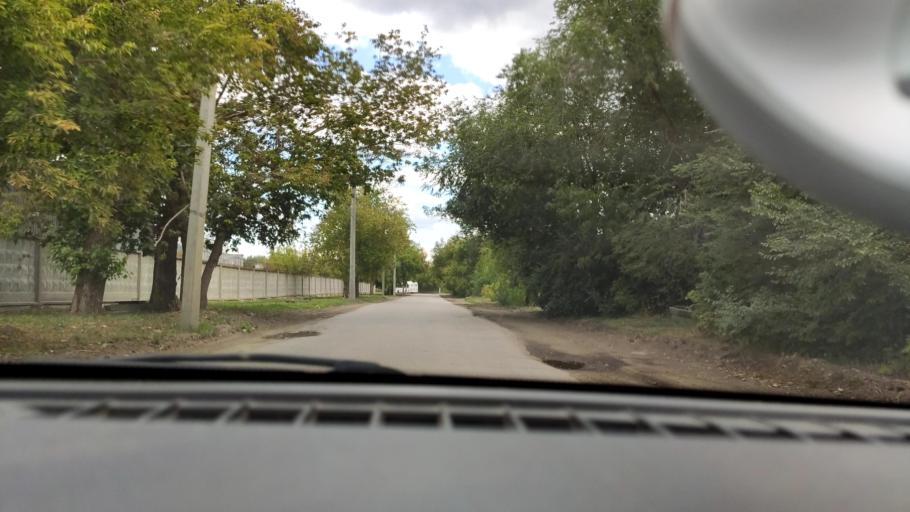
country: RU
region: Samara
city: Novokuybyshevsk
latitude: 53.1058
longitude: 50.0399
